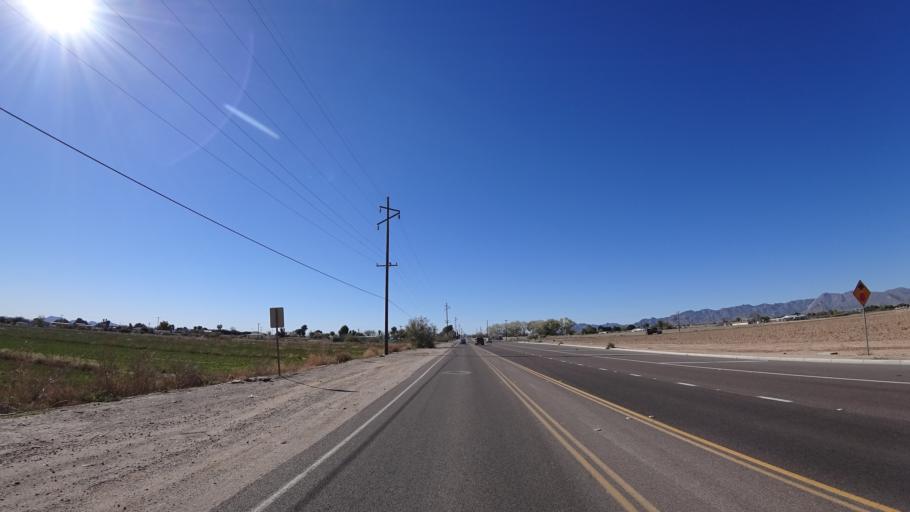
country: US
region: Arizona
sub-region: Maricopa County
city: Goodyear
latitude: 33.4356
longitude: -112.4426
